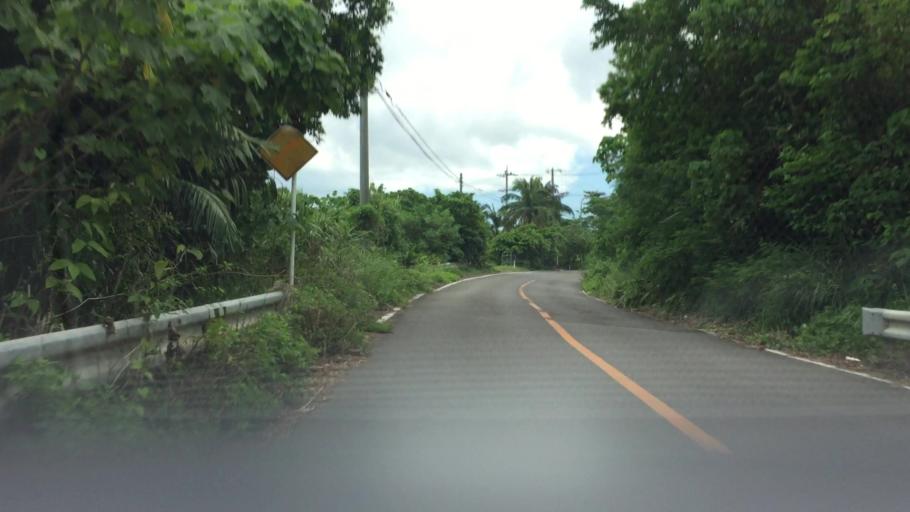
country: JP
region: Okinawa
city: Ishigaki
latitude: 24.3773
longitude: 124.1312
